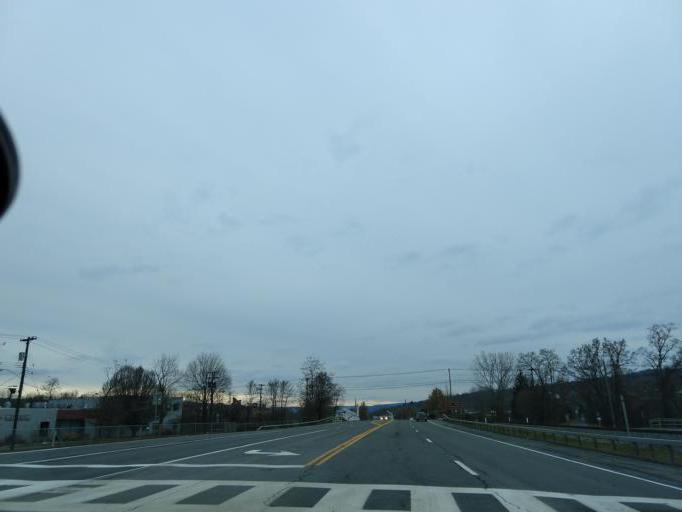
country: US
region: New York
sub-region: Tompkins County
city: Ithaca
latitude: 42.4516
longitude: -76.5034
